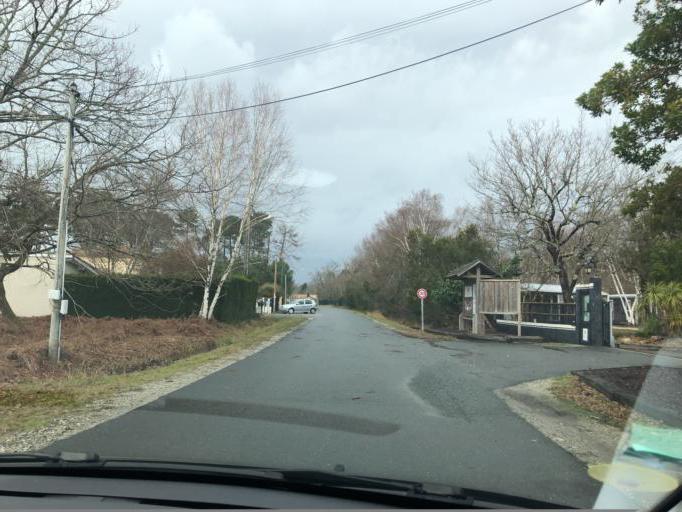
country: FR
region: Aquitaine
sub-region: Departement de la Gironde
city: Hourtin
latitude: 45.1790
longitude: -1.0749
